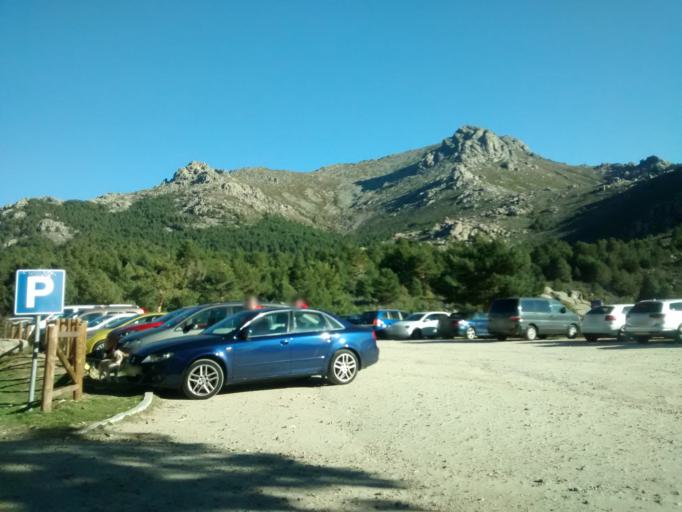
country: ES
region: Madrid
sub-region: Provincia de Madrid
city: Navacerrada
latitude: 40.7519
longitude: -3.9932
